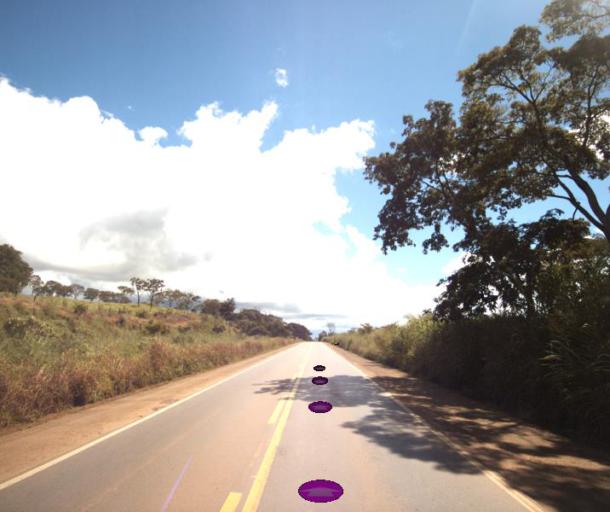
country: BR
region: Goias
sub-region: Anapolis
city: Anapolis
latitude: -16.1715
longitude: -49.0431
